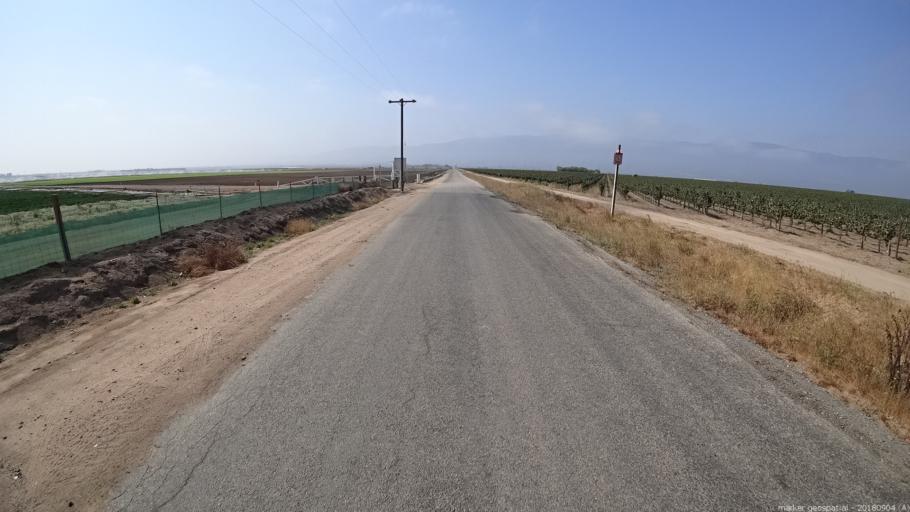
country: US
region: California
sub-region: Monterey County
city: Soledad
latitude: 36.4706
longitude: -121.3506
